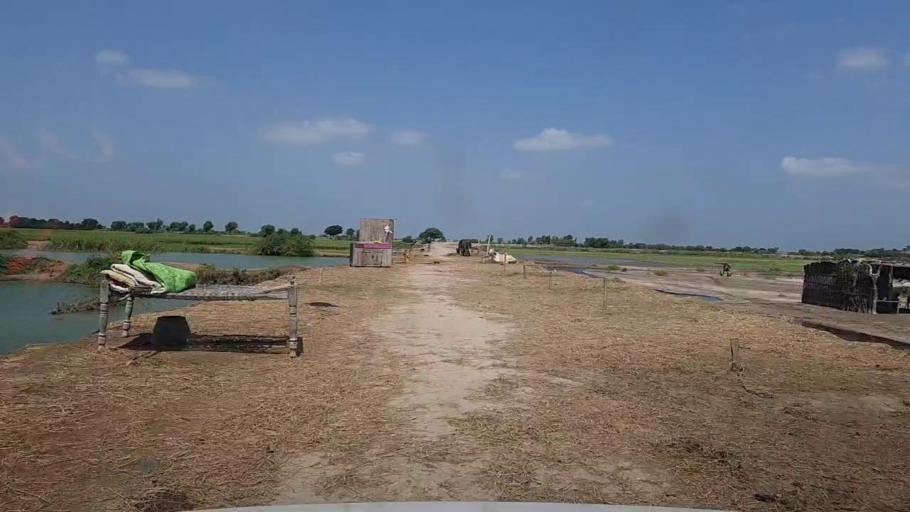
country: PK
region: Sindh
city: Kario
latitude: 24.6979
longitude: 68.5860
